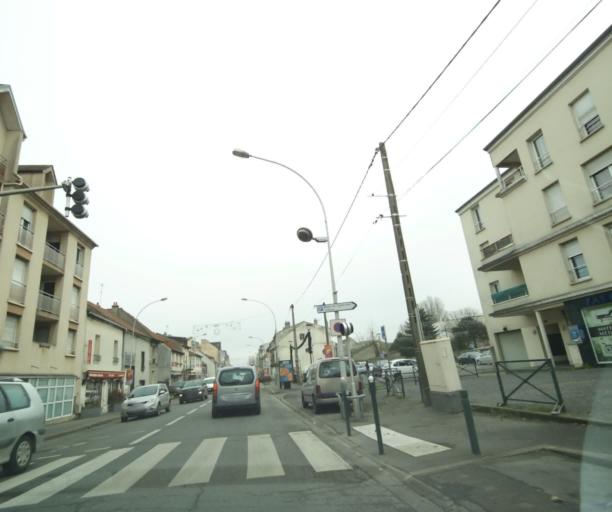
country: FR
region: Ile-de-France
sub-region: Departement de Seine-Saint-Denis
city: Vaujours
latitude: 48.9349
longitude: 2.5686
